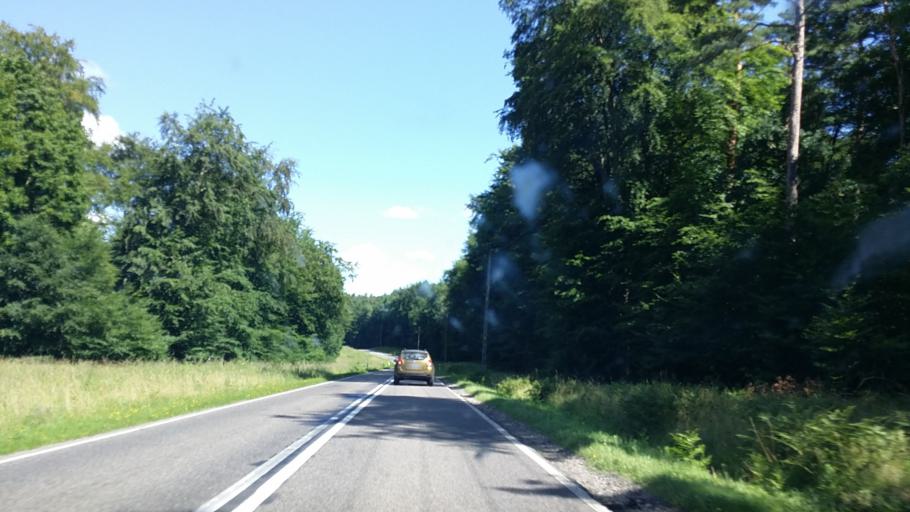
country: PL
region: West Pomeranian Voivodeship
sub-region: Powiat drawski
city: Drawsko Pomorskie
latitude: 53.4658
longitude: 15.8249
